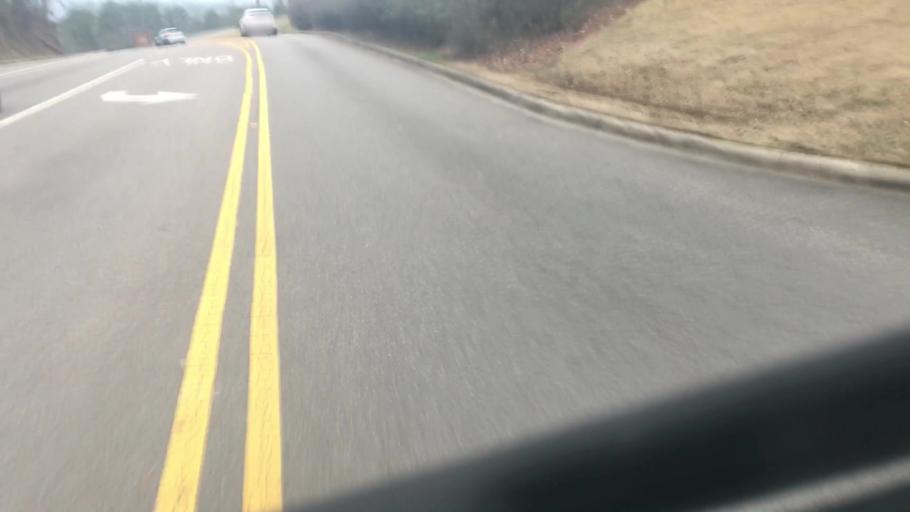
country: US
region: Alabama
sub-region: Shelby County
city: Indian Springs Village
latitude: 33.3550
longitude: -86.8041
